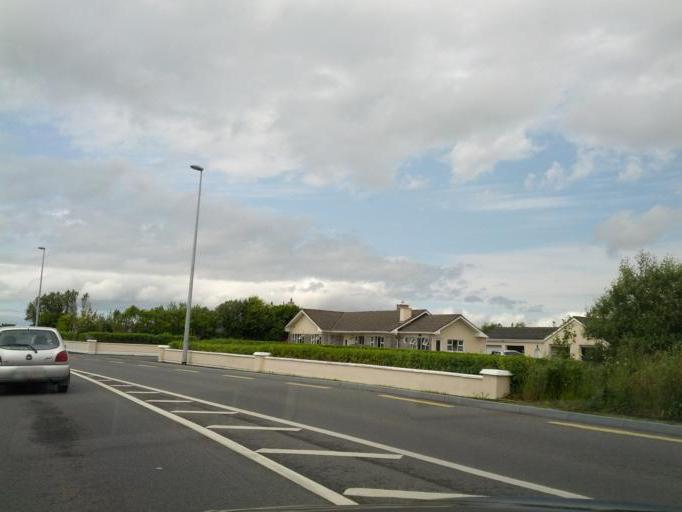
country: IE
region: Munster
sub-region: An Clar
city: Kilrush
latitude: 52.6450
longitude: -9.4934
